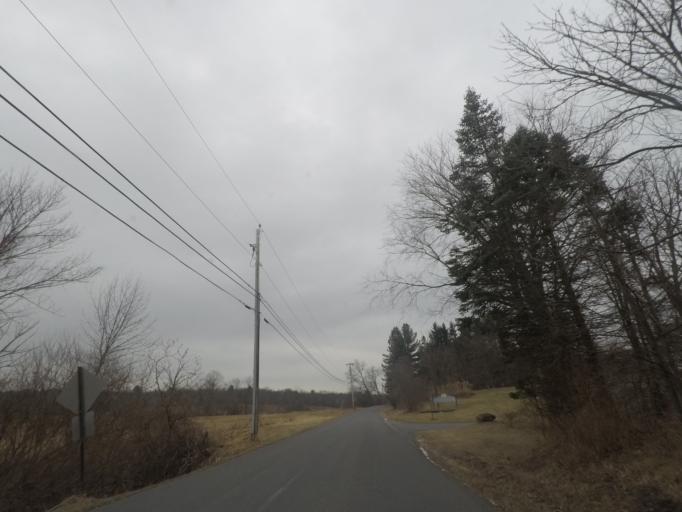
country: US
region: New York
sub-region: Rensselaer County
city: East Greenbush
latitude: 42.5617
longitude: -73.6537
